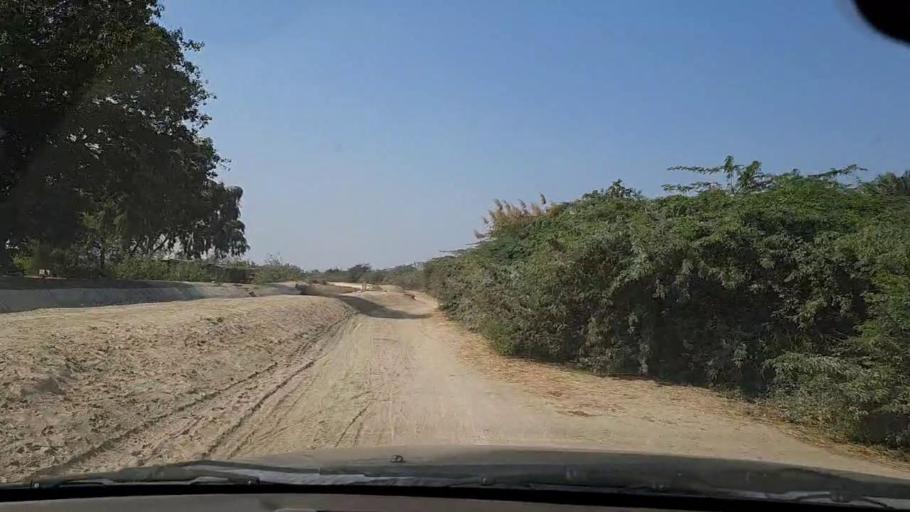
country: PK
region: Sindh
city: Chuhar Jamali
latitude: 24.4267
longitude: 67.8130
